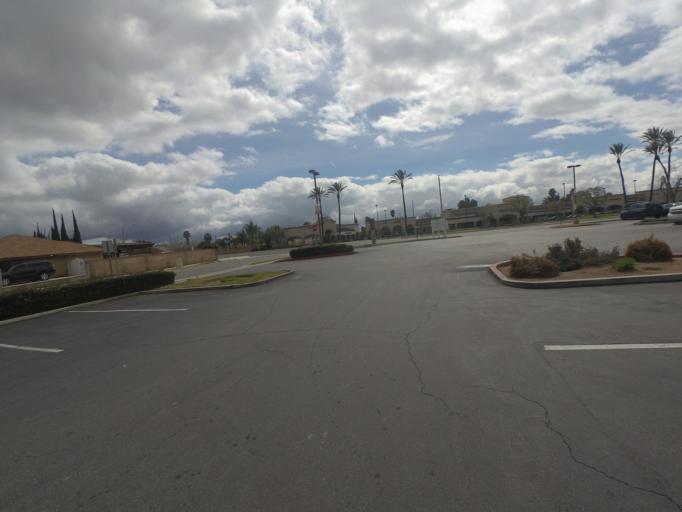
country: US
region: California
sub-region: Riverside County
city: Moreno Valley
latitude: 33.9179
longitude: -117.2422
